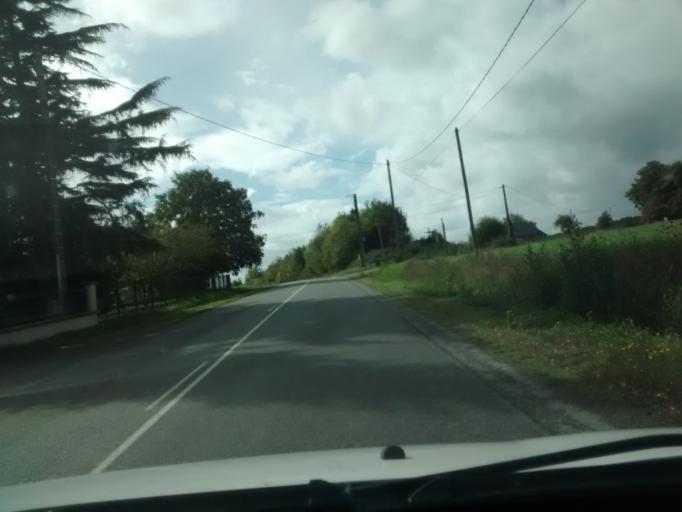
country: FR
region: Brittany
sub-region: Departement d'Ille-et-Vilaine
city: Saint-Didier
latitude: 48.1401
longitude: -1.3520
